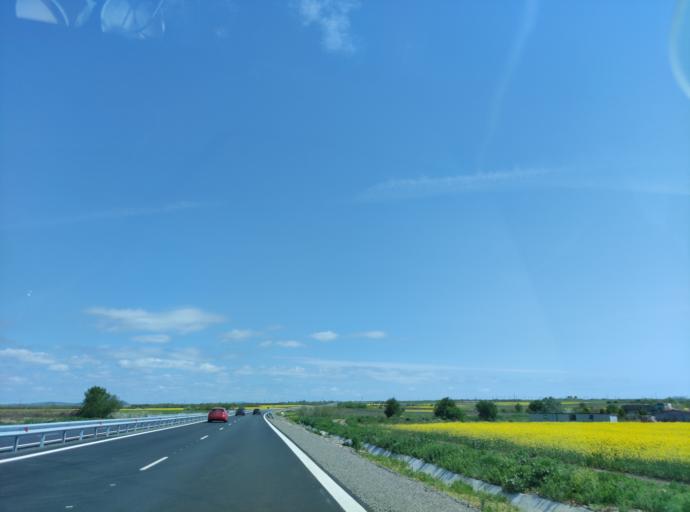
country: BG
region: Burgas
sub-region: Obshtina Pomorie
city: Pomorie
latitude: 42.5695
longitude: 27.5735
